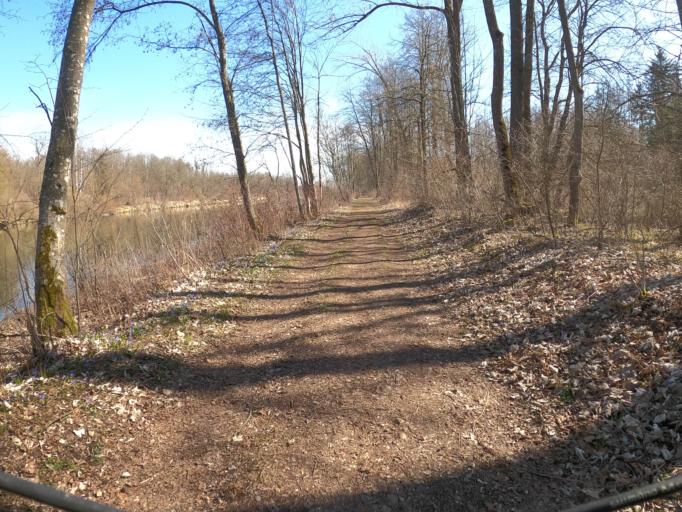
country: DE
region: Bavaria
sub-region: Swabia
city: Nersingen
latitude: 48.4416
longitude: 10.1264
